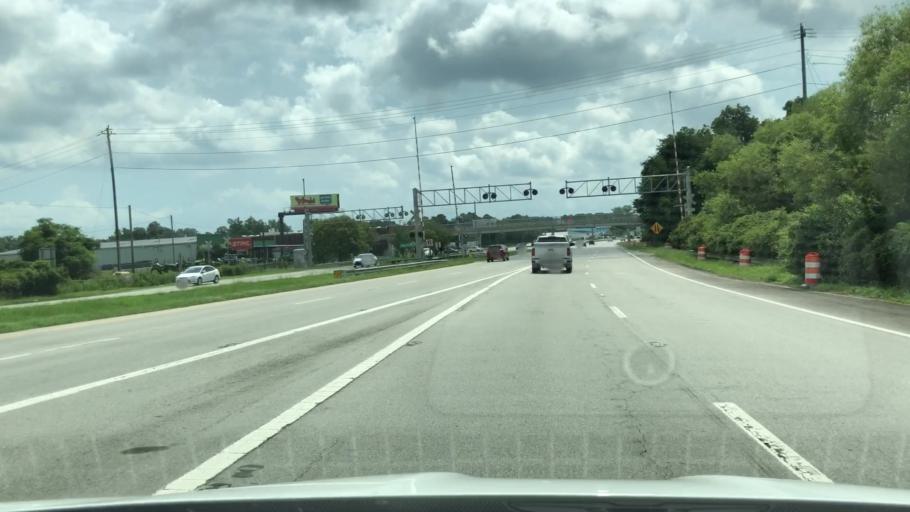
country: US
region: North Carolina
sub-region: Craven County
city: James City
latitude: 35.0890
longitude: -77.0355
